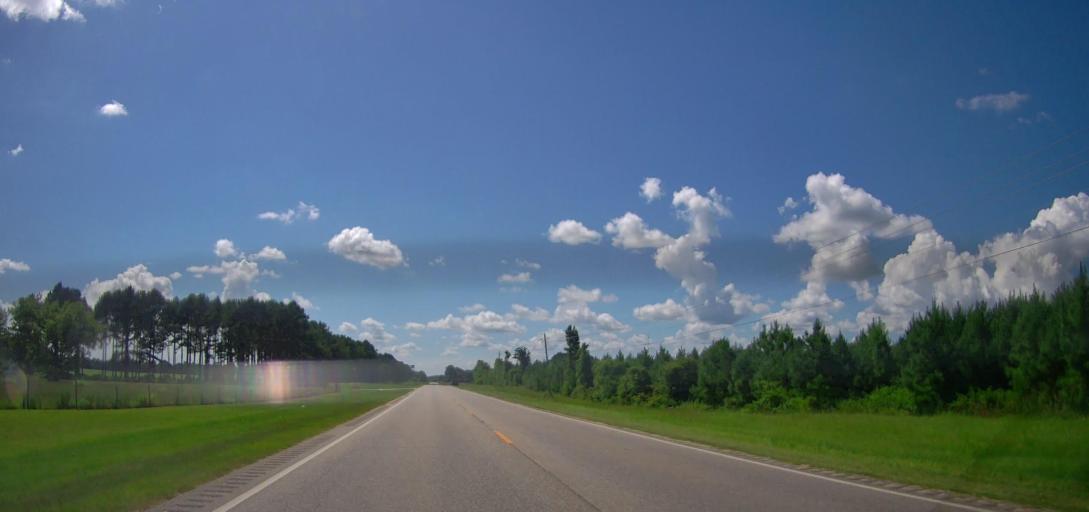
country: US
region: Alabama
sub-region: Elmore County
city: Tallassee
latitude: 32.3887
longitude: -85.8908
